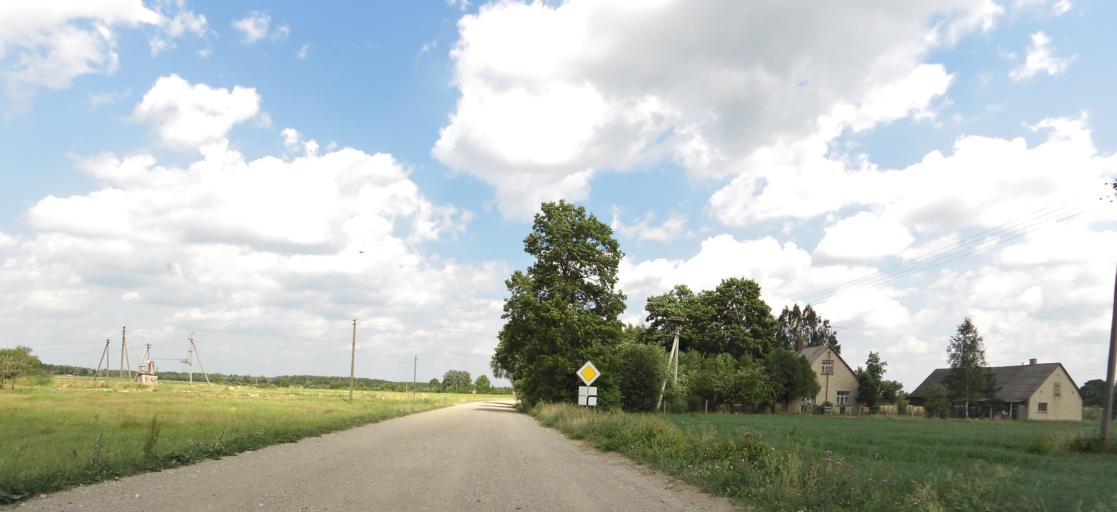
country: LT
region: Panevezys
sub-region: Birzai
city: Birzai
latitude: 56.1177
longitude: 24.8877
